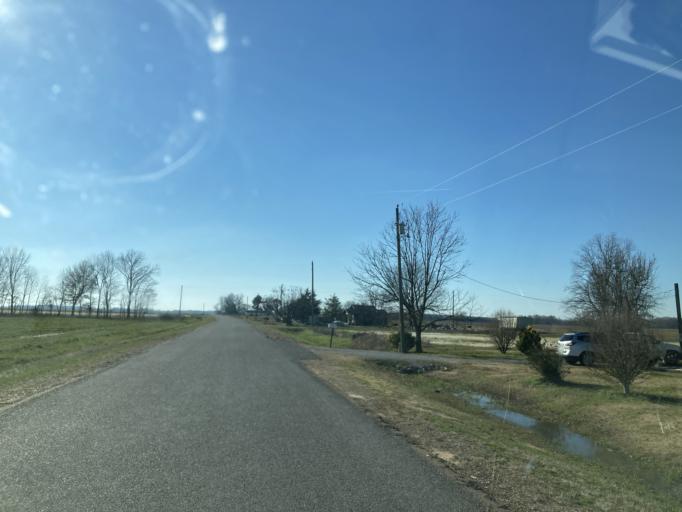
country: US
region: Mississippi
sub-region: Yazoo County
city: Yazoo City
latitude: 32.9649
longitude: -90.6056
